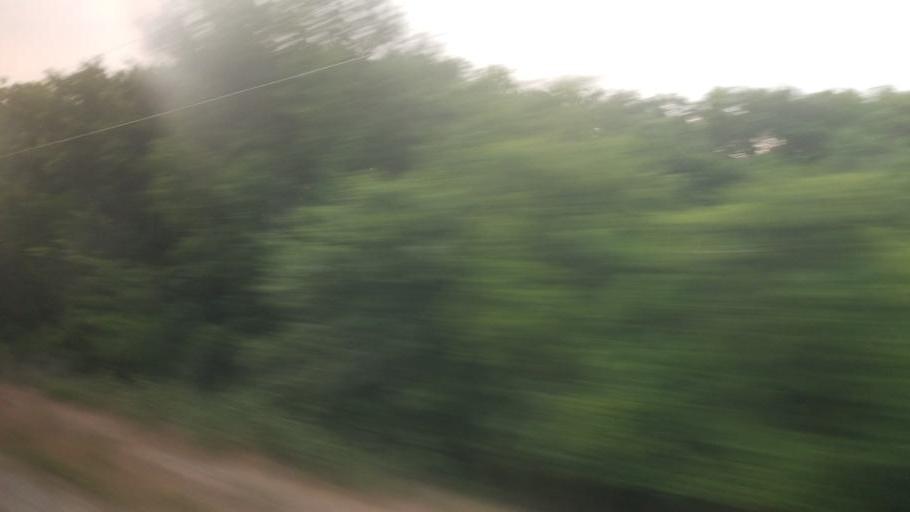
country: US
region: Kansas
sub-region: Marion County
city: Peabody
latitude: 38.1679
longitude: -97.0709
